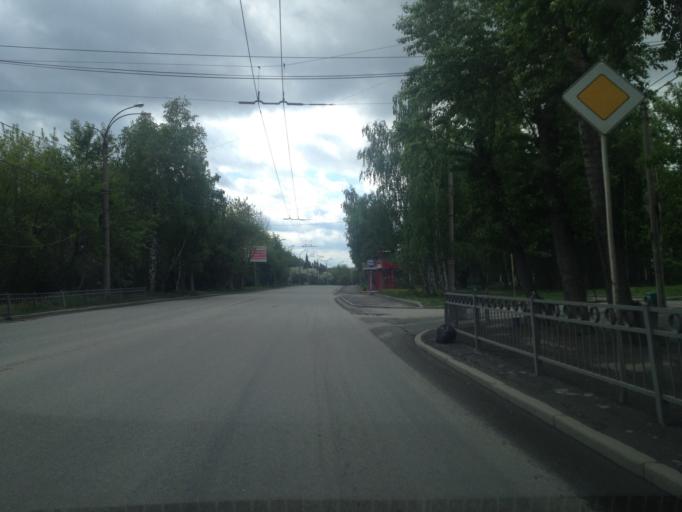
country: RU
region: Sverdlovsk
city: Yekaterinburg
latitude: 56.7737
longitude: 60.6673
